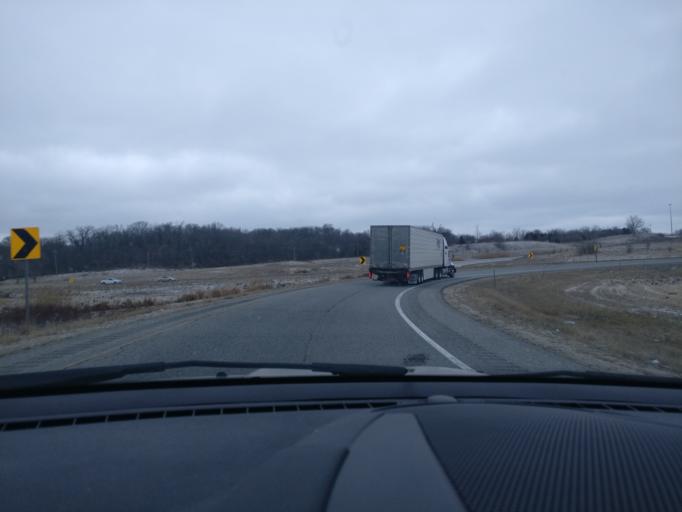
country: US
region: Illinois
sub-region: Henry County
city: Colona
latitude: 41.5345
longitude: -90.3441
